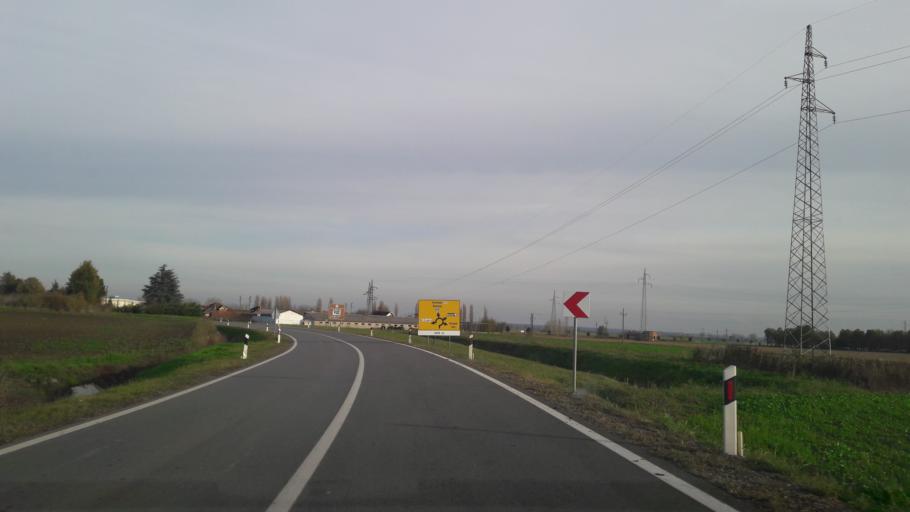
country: HR
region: Osjecko-Baranjska
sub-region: Grad Osijek
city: Karanac
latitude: 45.7418
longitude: 18.7215
